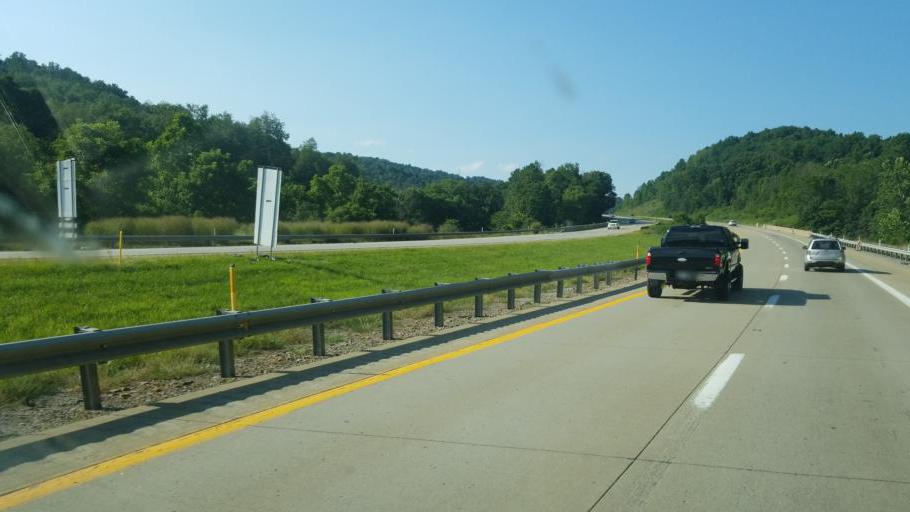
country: US
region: West Virginia
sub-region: Monongalia County
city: Star City
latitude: 39.7681
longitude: -80.0804
